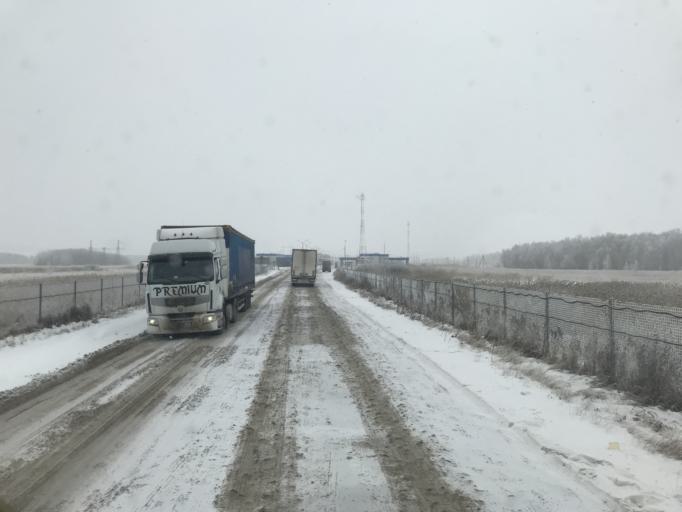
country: RU
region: Kurgan
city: Petukhovo
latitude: 55.0915
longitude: 68.2496
